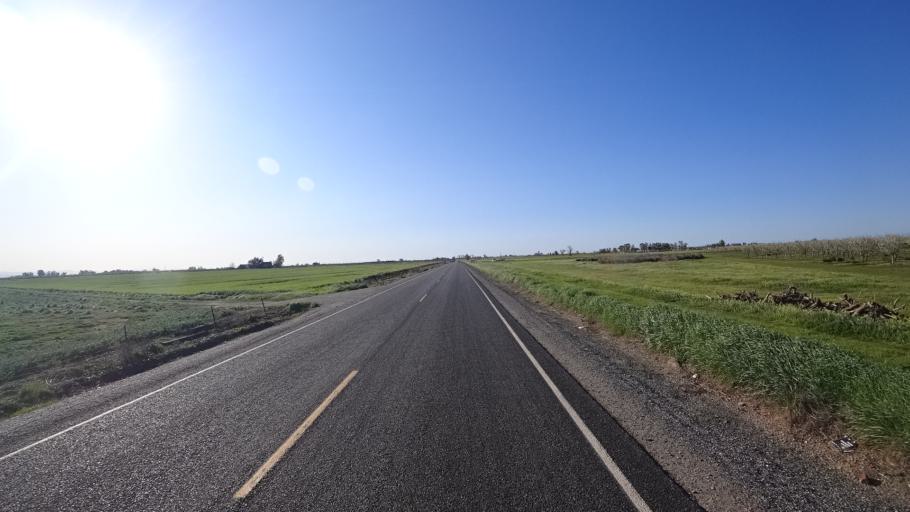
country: US
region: California
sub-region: Glenn County
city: Orland
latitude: 39.7852
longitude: -122.1186
